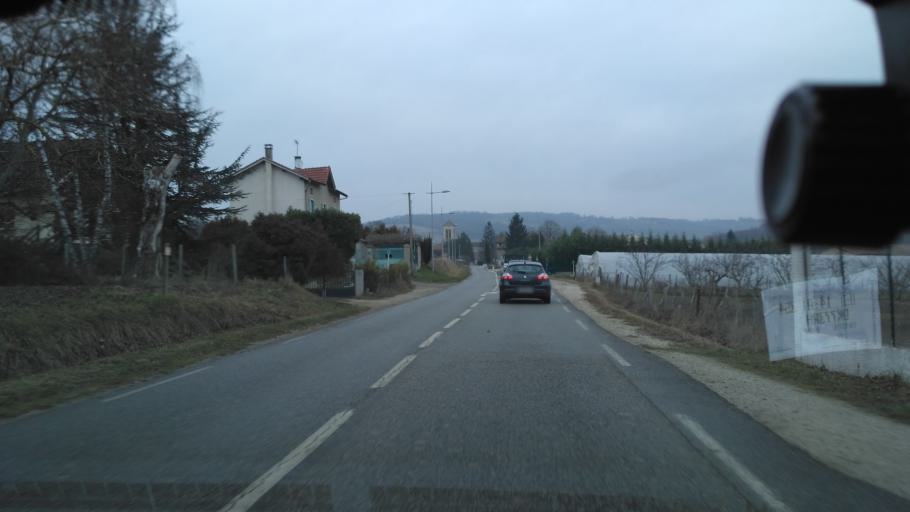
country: FR
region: Rhone-Alpes
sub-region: Departement de la Drome
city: Genissieux
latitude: 45.1413
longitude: 5.1182
